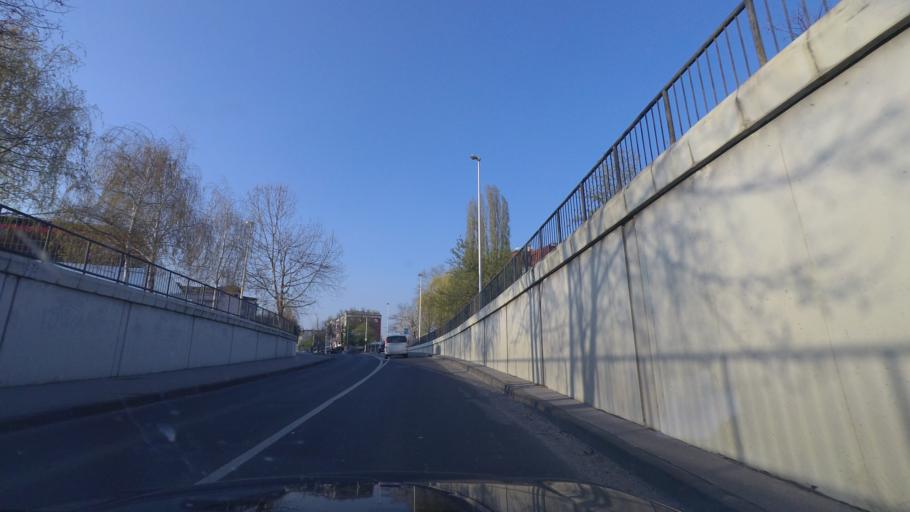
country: HR
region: Grad Zagreb
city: Dubrava
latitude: 45.8217
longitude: 16.0640
